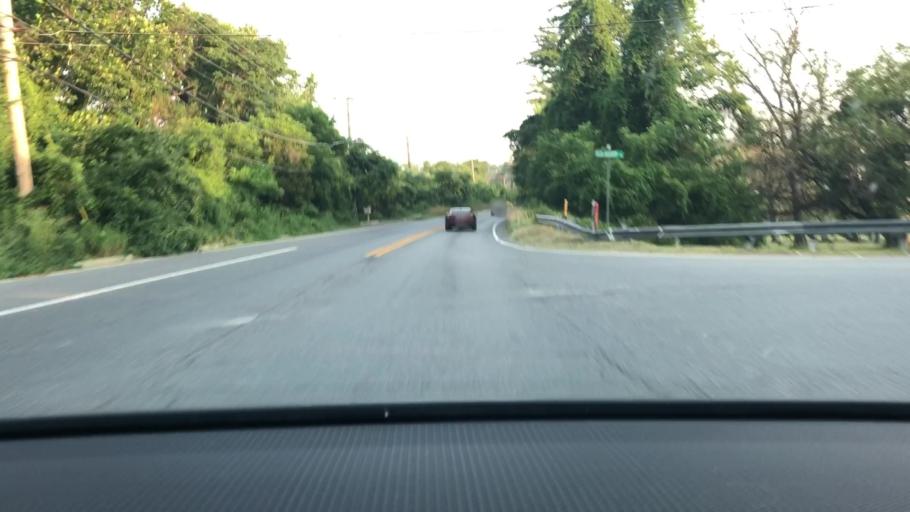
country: US
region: Maryland
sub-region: Anne Arundel County
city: Jessup
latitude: 39.1491
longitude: -76.7751
